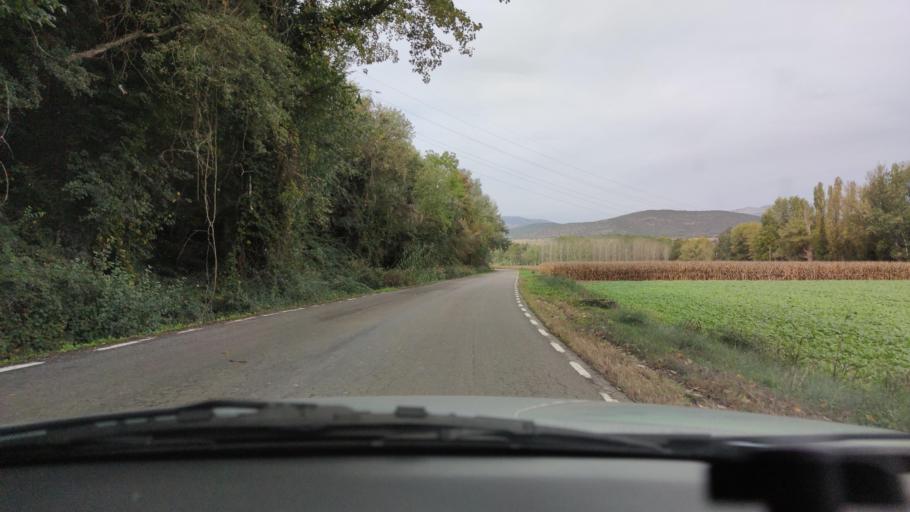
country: ES
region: Catalonia
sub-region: Provincia de Lleida
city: Artesa de Segre
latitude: 41.9175
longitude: 1.0982
